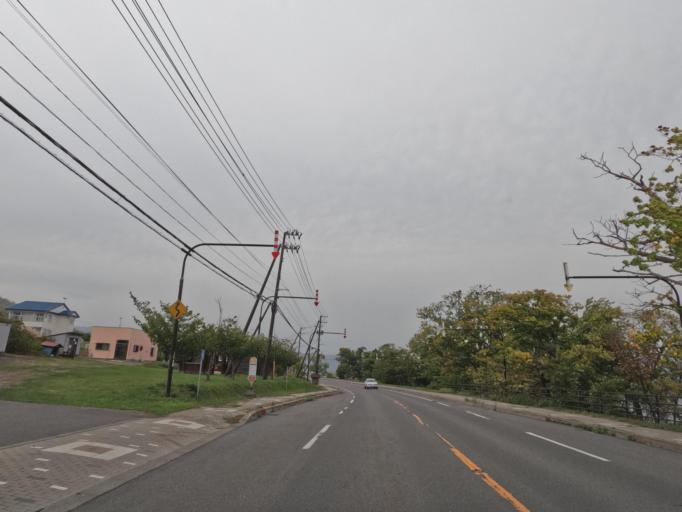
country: JP
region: Hokkaido
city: Date
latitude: 42.5590
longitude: 140.8540
